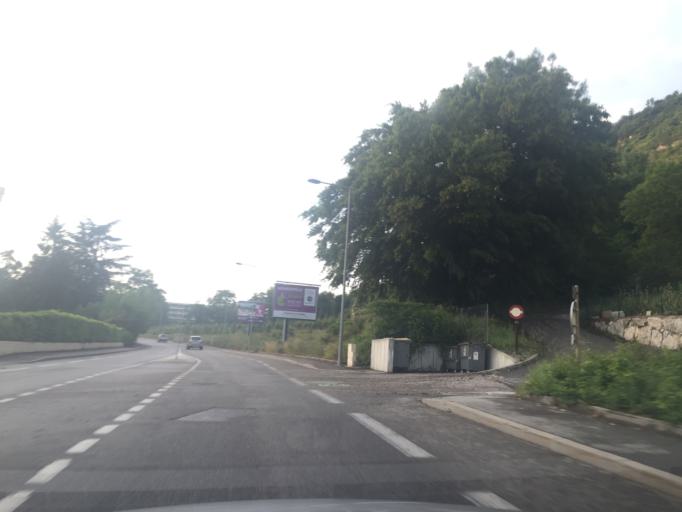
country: FR
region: Rhone-Alpes
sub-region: Departement de la Savoie
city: Chambery
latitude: 45.5833
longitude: 5.9244
